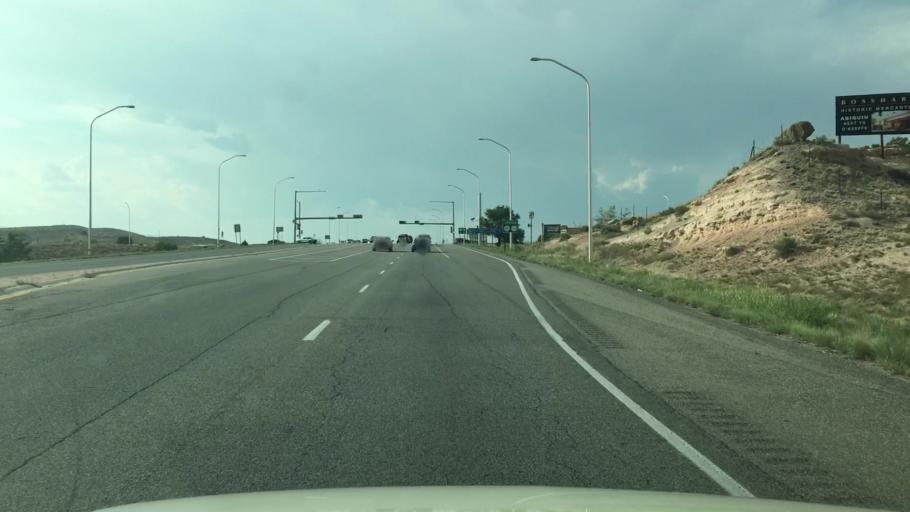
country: US
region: New Mexico
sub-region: Santa Fe County
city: El Valle de Arroyo Seco
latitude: 35.9747
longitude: -106.0428
